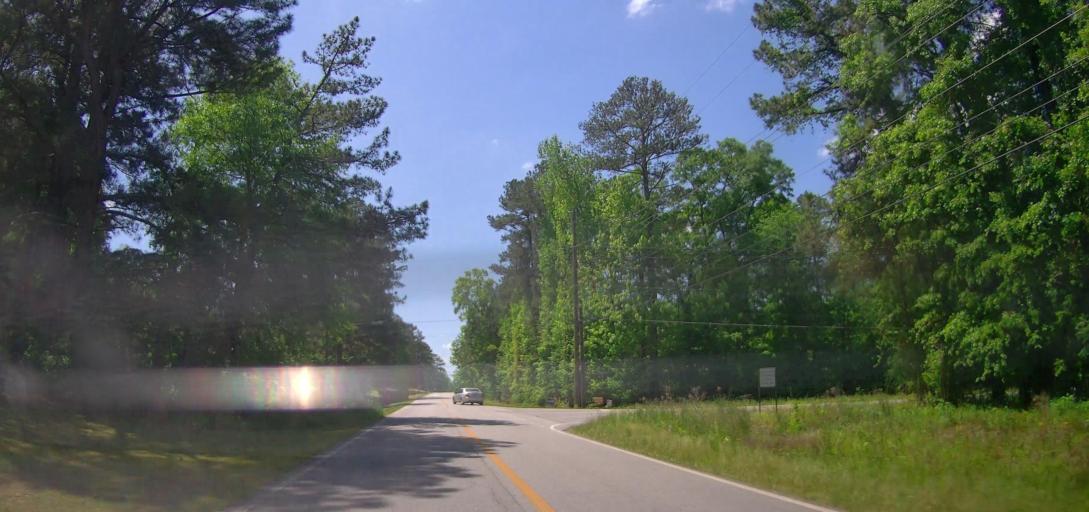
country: US
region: Georgia
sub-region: Bibb County
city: Macon
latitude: 32.8952
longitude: -83.6074
